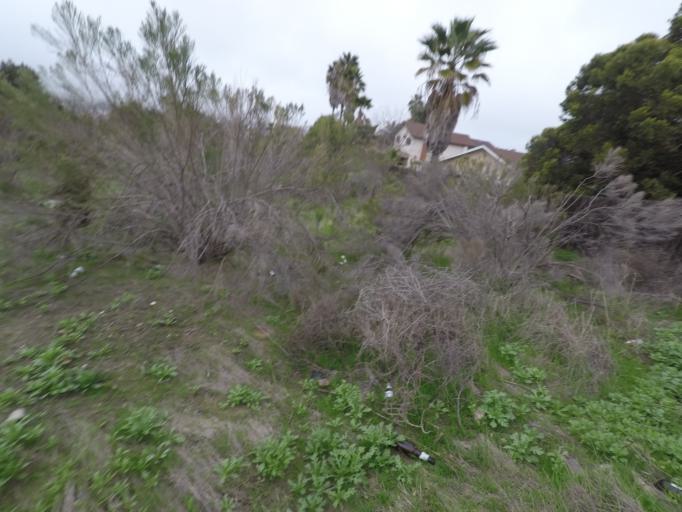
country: MX
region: Baja California
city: Tijuana
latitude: 32.5569
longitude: -117.0386
